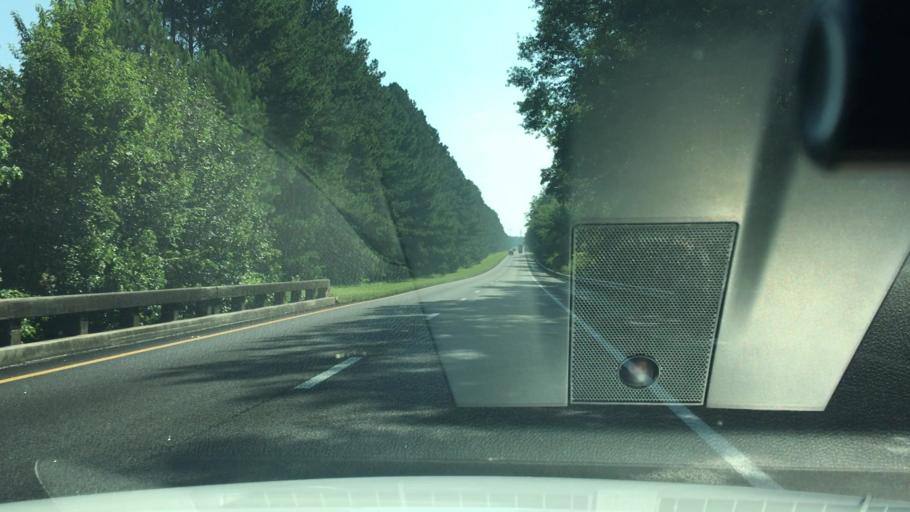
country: US
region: South Carolina
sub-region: Aiken County
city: Graniteville
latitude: 33.6280
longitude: -81.8067
